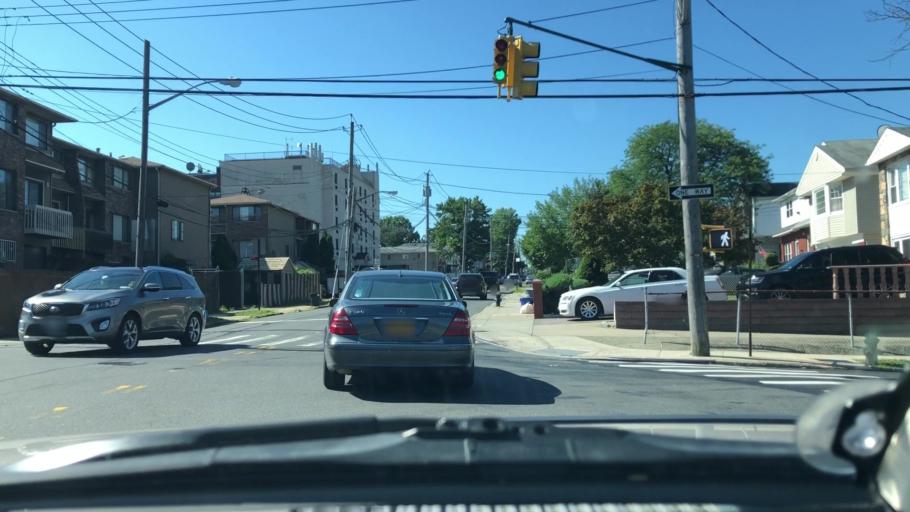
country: US
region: New York
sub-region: Richmond County
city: Staten Island
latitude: 40.6079
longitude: -74.1322
